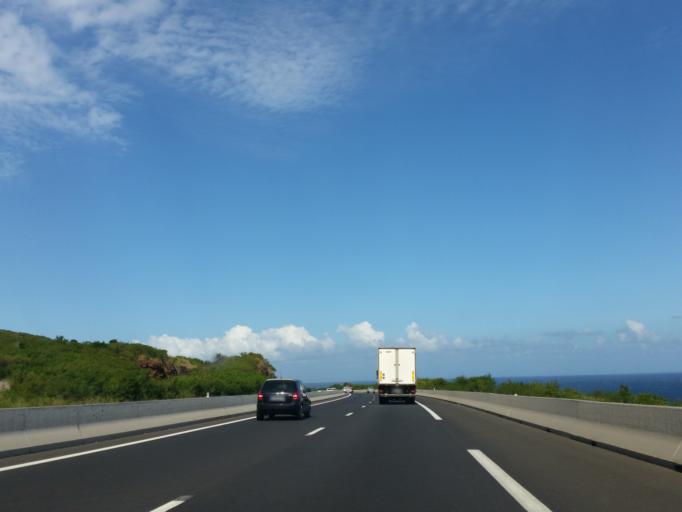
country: RE
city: Piton Saint-Leu
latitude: -21.2390
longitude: 55.3150
